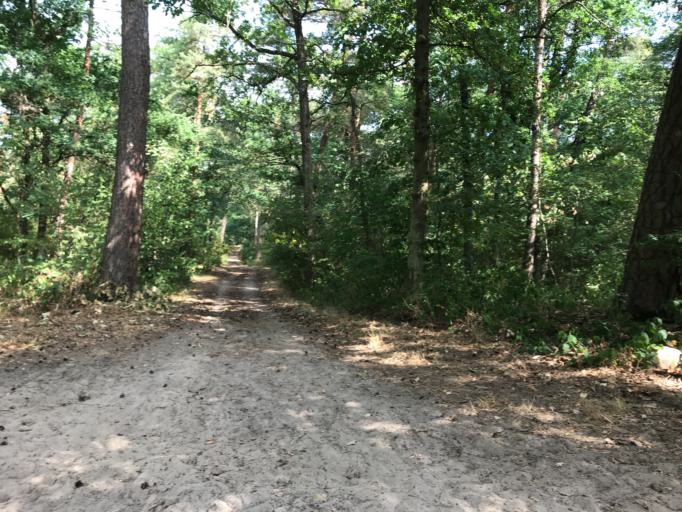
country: DE
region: Rheinland-Pfalz
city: Budenheim
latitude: 50.0090
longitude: 8.1579
